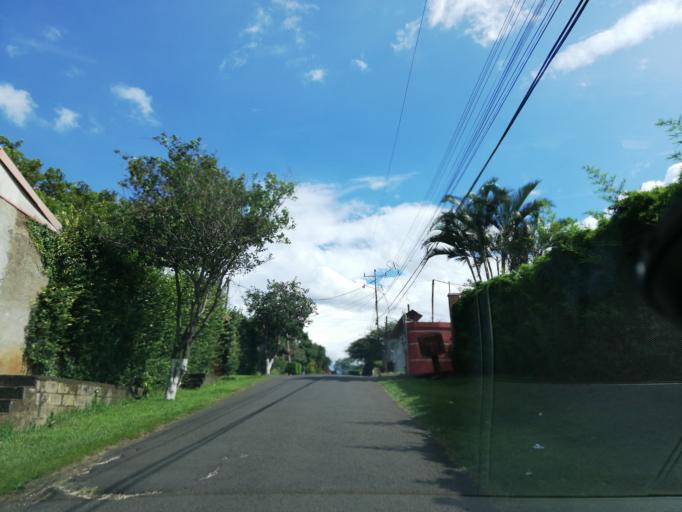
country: CR
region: Alajuela
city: Alajuela
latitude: 9.9837
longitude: -84.2190
